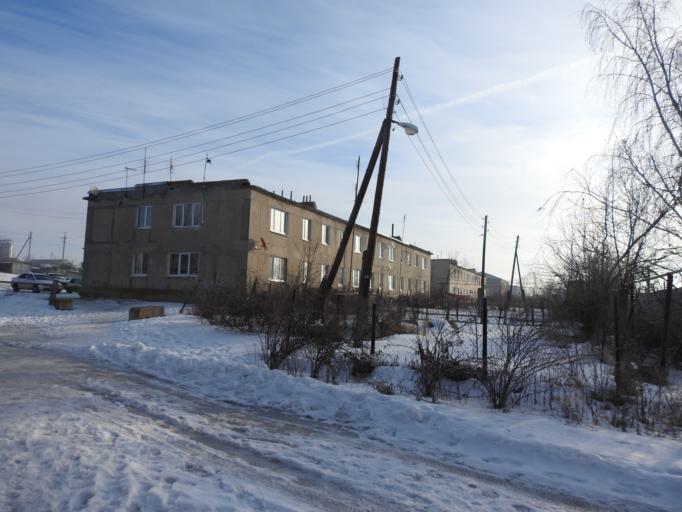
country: RU
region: Saratov
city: Krasnyy Oktyabr'
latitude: 51.4965
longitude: 45.7181
